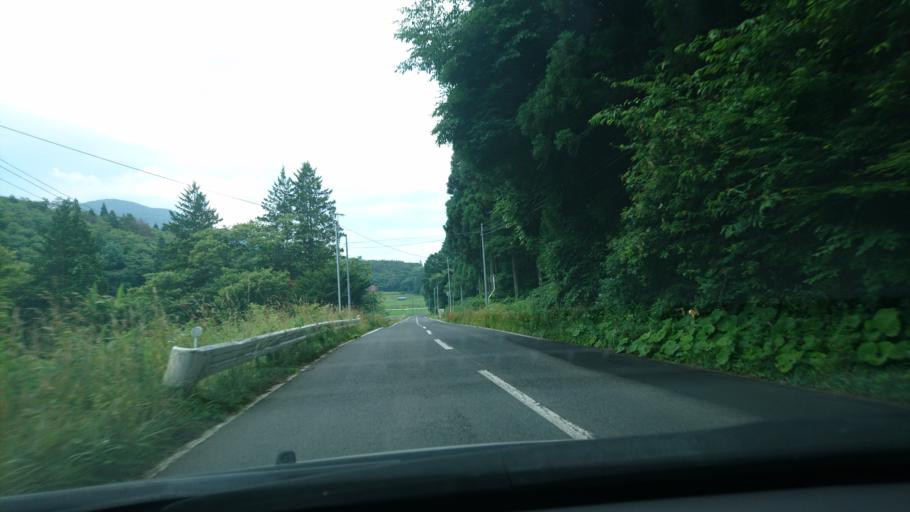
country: JP
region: Iwate
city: Ichinoseki
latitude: 38.8818
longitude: 141.4256
